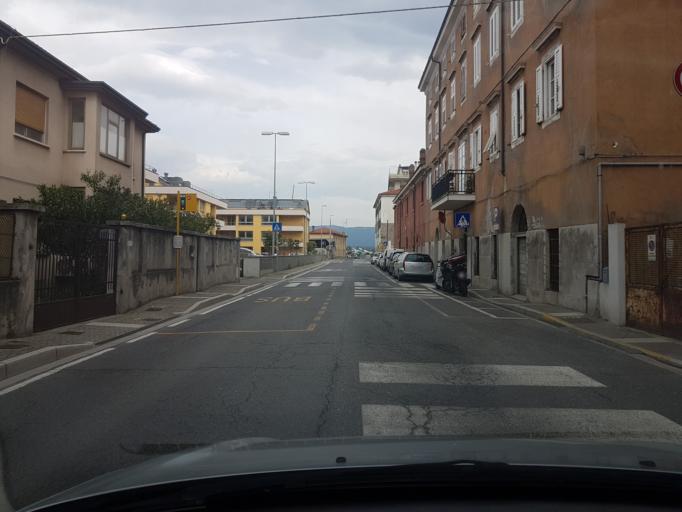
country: IT
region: Friuli Venezia Giulia
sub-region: Provincia di Trieste
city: Muggia
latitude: 45.6040
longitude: 13.7711
